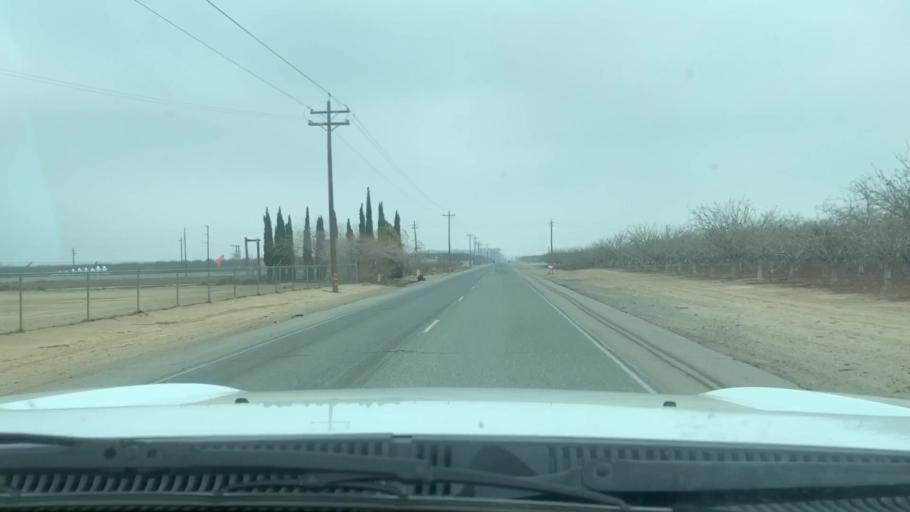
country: US
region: California
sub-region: Kern County
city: Buttonwillow
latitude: 35.5006
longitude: -119.4959
